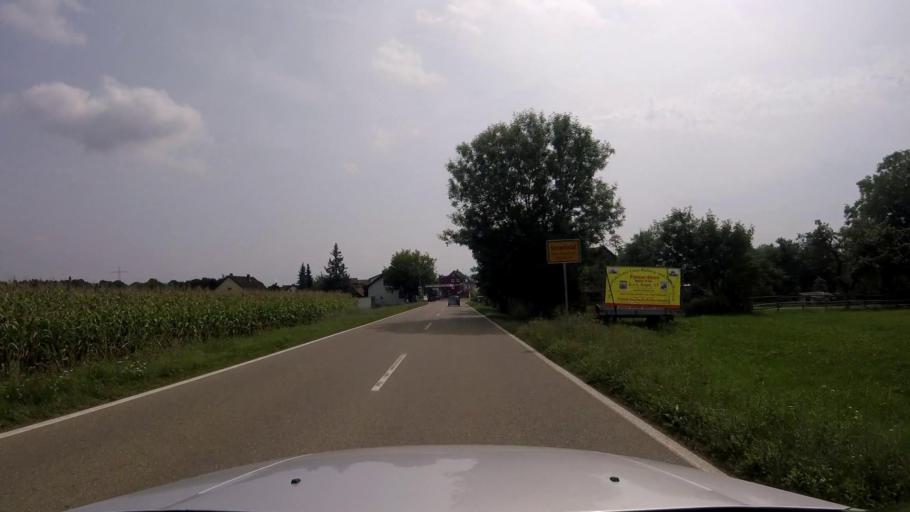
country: DE
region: Baden-Wuerttemberg
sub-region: Regierungsbezirk Stuttgart
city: Spraitbach
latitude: 48.8991
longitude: 9.7558
